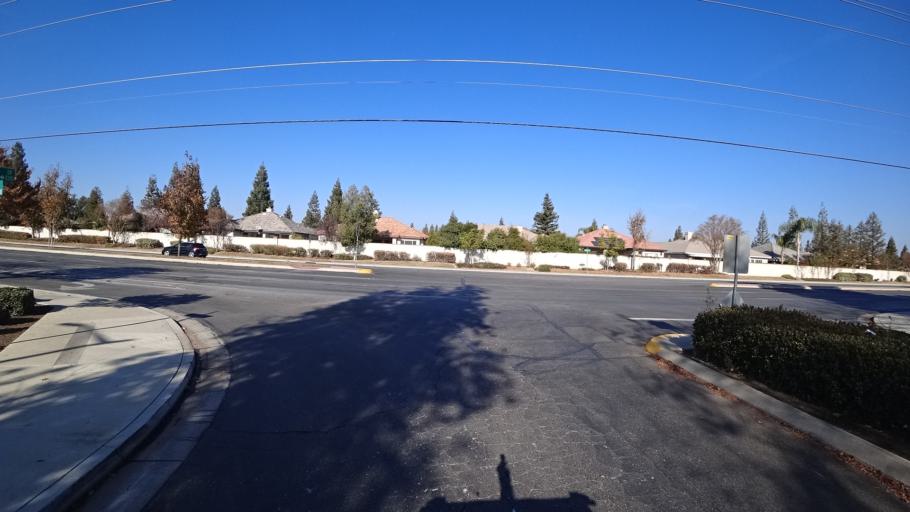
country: US
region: California
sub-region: Kern County
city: Greenacres
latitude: 35.3250
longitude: -119.1135
